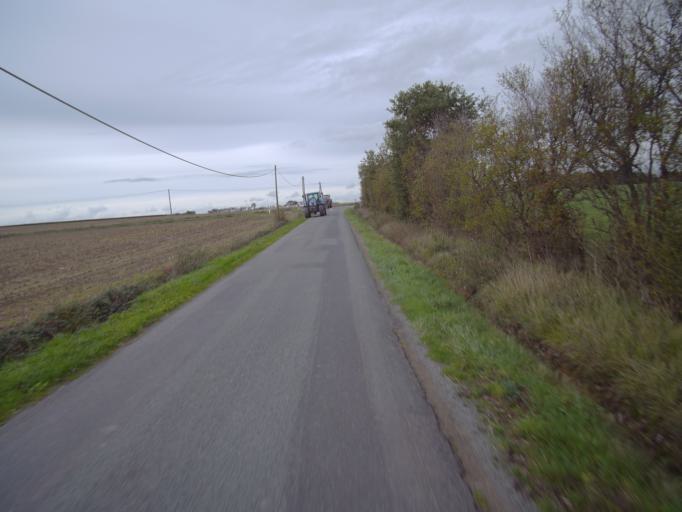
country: FR
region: Pays de la Loire
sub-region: Departement de la Loire-Atlantique
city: Remouille
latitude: 47.0387
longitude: -1.3963
